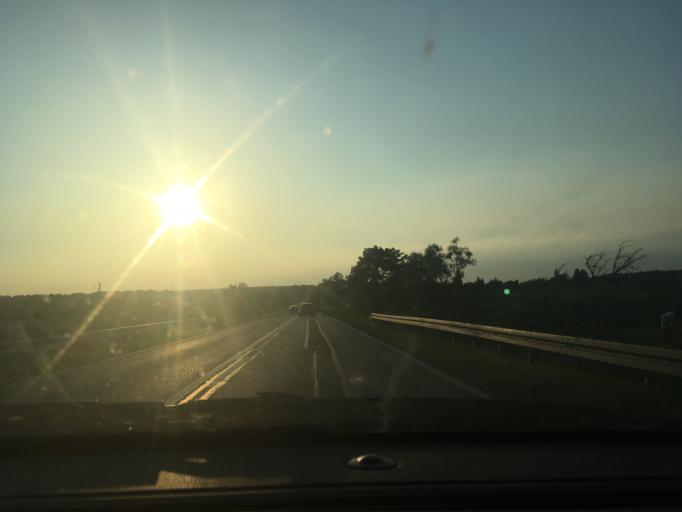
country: PL
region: Podlasie
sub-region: Powiat moniecki
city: Goniadz
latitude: 53.4834
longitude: 22.6373
